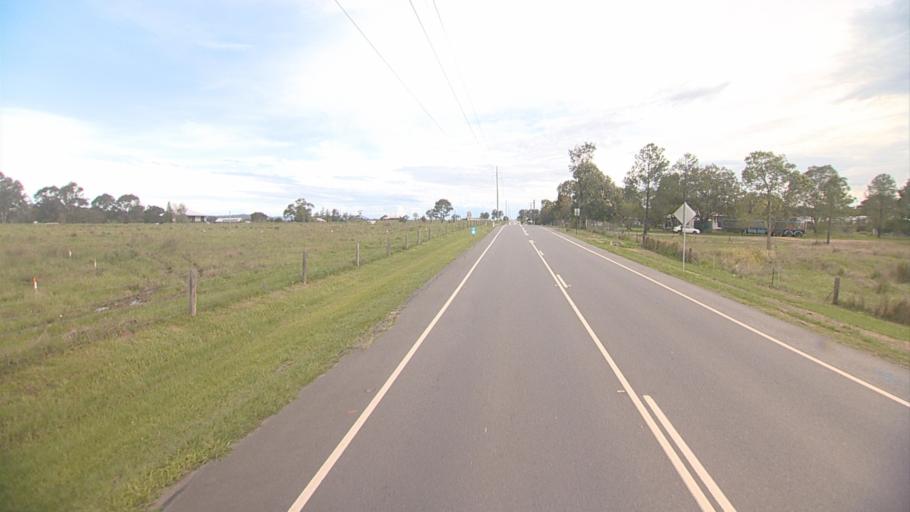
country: AU
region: Queensland
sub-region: Logan
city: Waterford West
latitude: -27.7063
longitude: 153.1171
